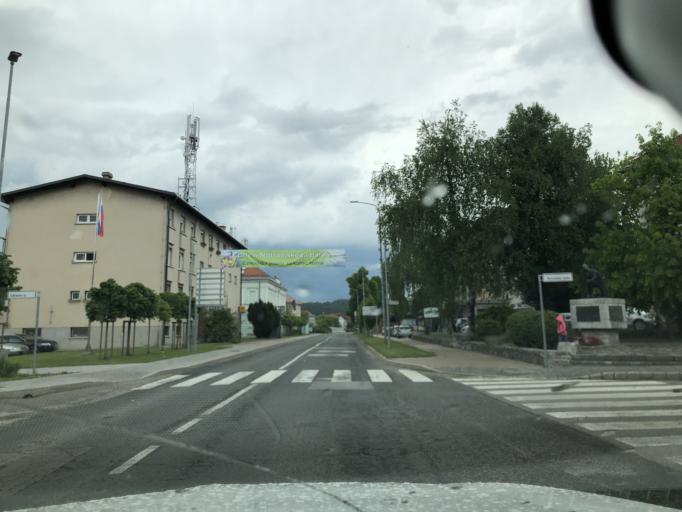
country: SI
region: Cerknica
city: Cerknica
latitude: 45.7933
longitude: 14.3629
